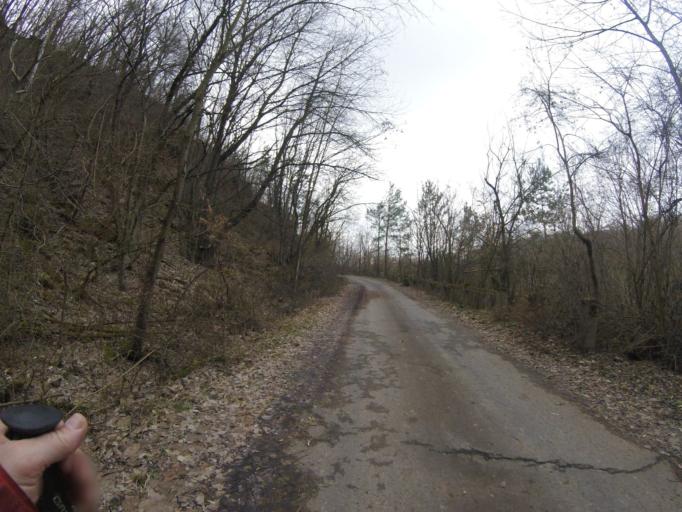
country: HU
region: Borsod-Abauj-Zemplen
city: Rudabanya
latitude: 48.3964
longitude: 20.6468
